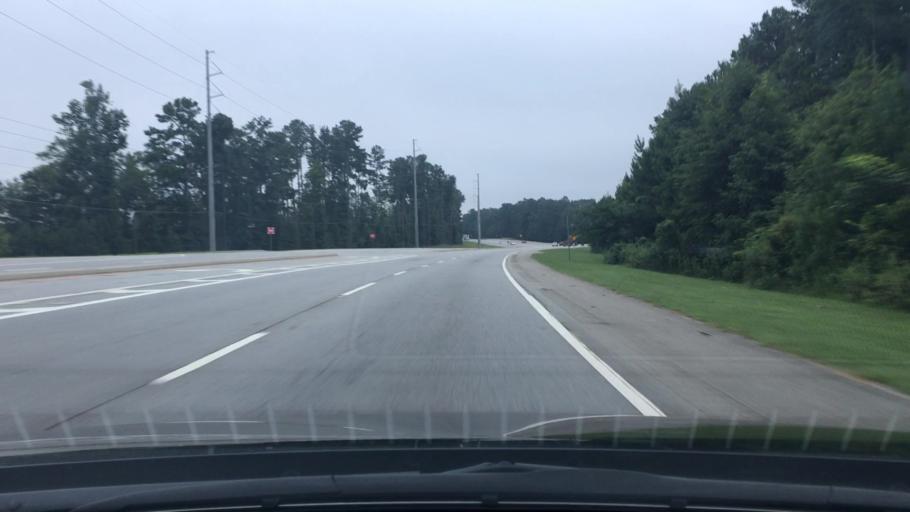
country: US
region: Georgia
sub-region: Coweta County
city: Senoia
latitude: 33.3481
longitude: -84.5489
